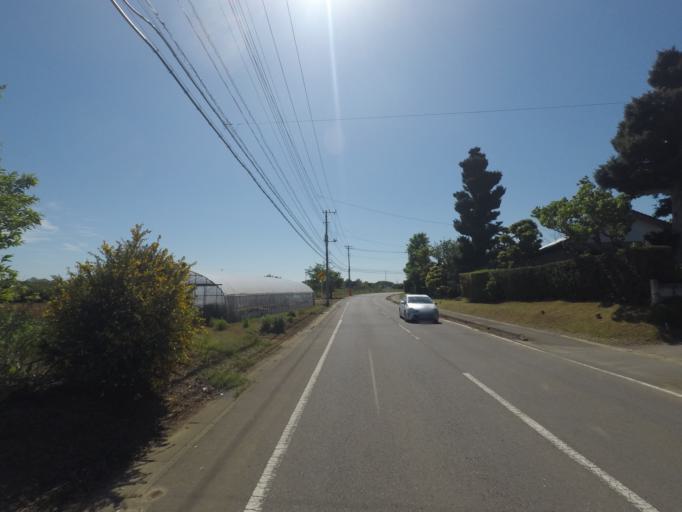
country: JP
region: Ibaraki
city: Itako
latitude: 36.0303
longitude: 140.4772
